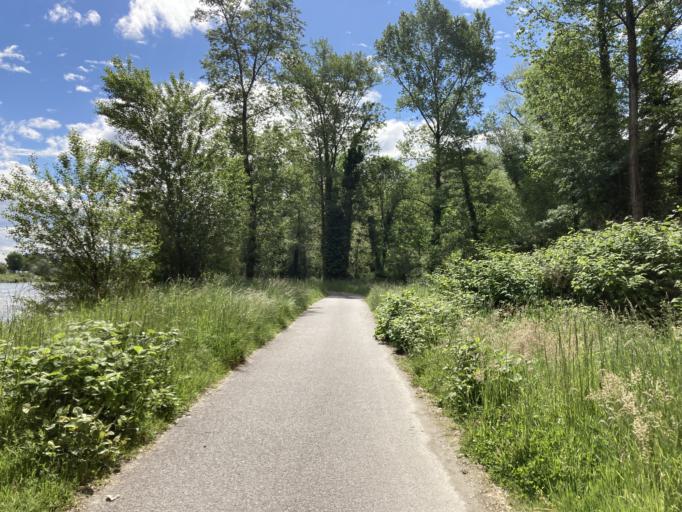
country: FR
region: Aquitaine
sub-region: Departement des Pyrenees-Atlantiques
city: Billere
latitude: 43.2998
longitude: -0.4215
